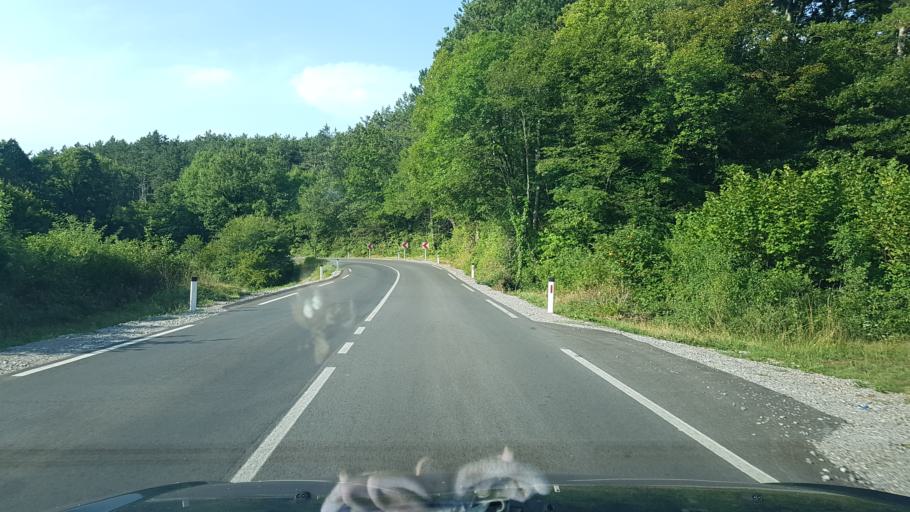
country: SI
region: Divaca
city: Divaca
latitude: 45.6681
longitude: 14.0184
